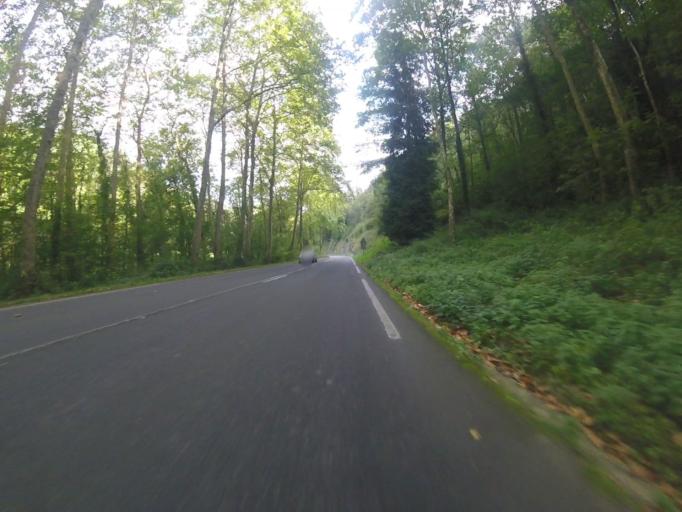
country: ES
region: Basque Country
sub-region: Provincia de Guipuzcoa
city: Orendain
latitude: 43.0775
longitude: -2.0879
